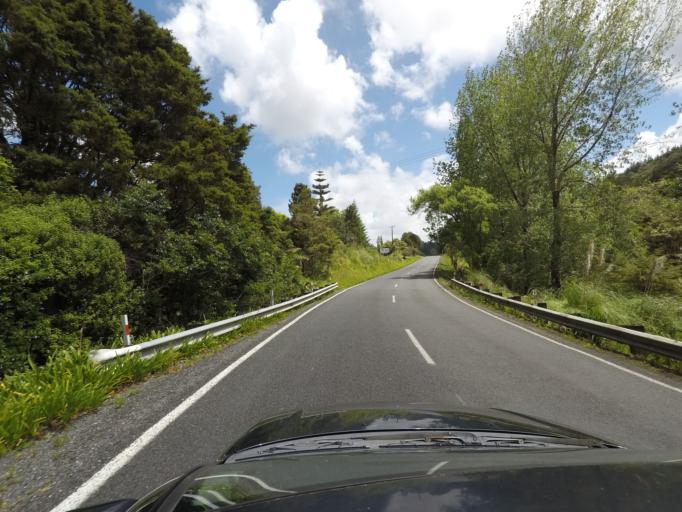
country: NZ
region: Auckland
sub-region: Auckland
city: Warkworth
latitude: -36.5039
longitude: 174.6401
